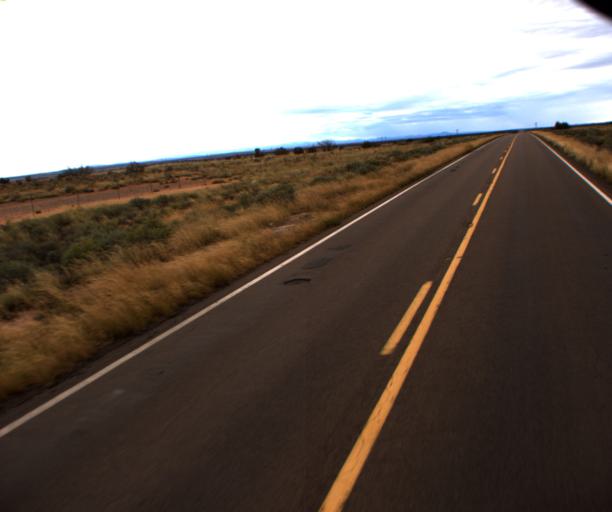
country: US
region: Arizona
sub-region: Navajo County
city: Snowflake
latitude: 34.6695
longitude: -110.1017
